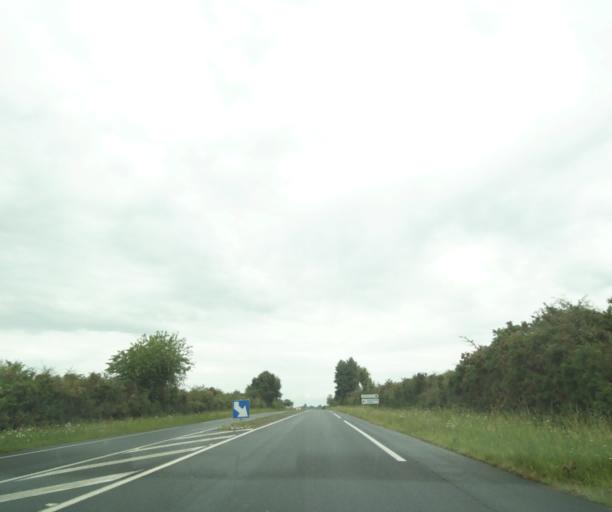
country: FR
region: Poitou-Charentes
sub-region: Departement des Deux-Sevres
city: Viennay
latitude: 46.7604
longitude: -0.2214
